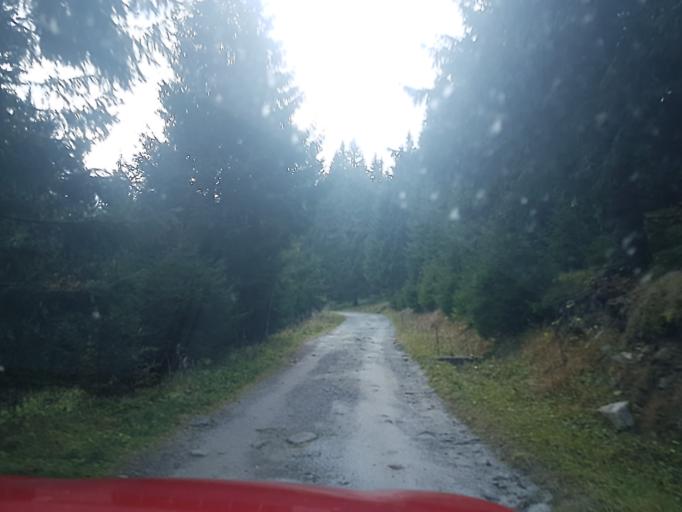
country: SK
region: Zilinsky
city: Ruzomberok
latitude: 48.9938
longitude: 19.2050
